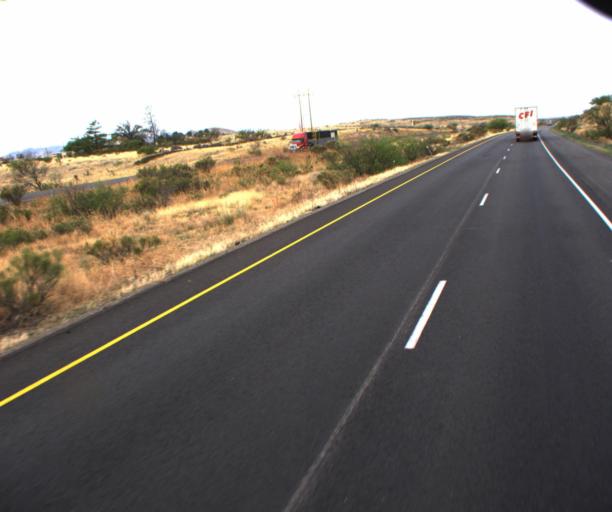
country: US
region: Arizona
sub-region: Cochise County
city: Mescal
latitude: 31.9644
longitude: -110.4558
